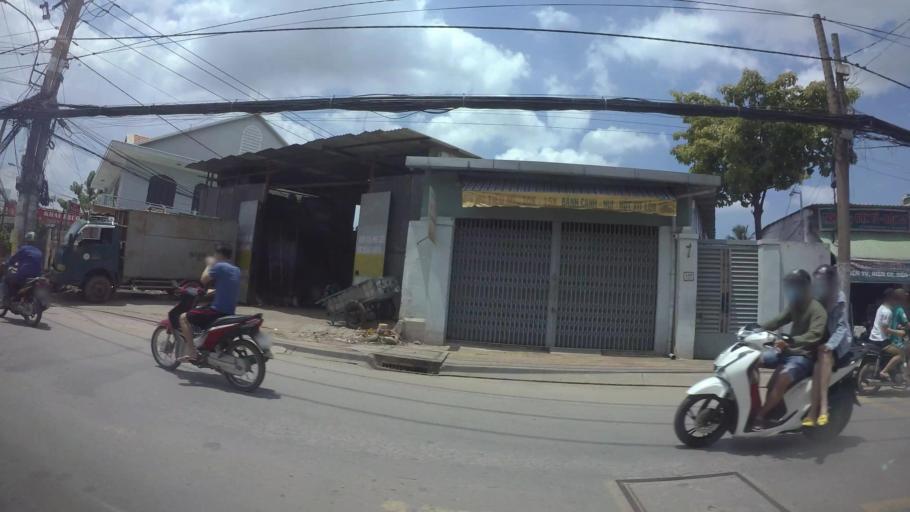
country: VN
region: Ho Chi Minh City
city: Quan Chin
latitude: 10.8365
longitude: 106.7822
